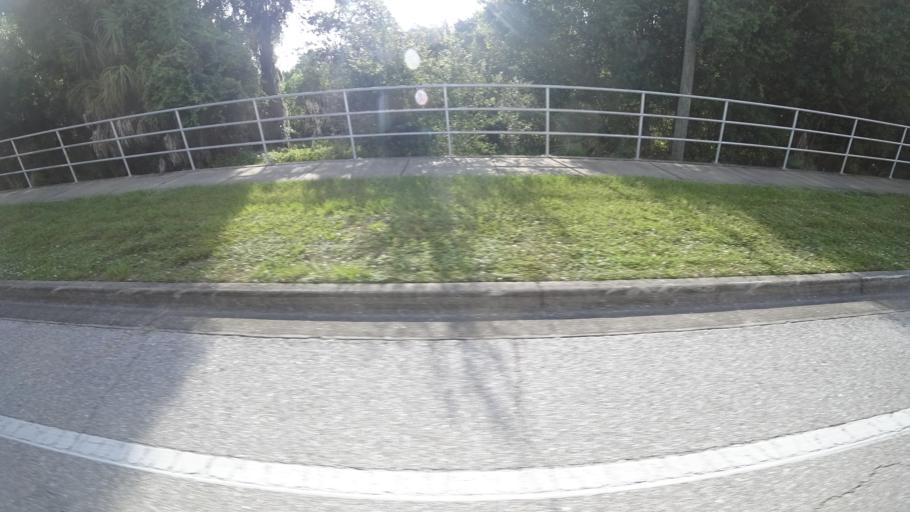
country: US
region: Florida
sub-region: Sarasota County
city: The Meadows
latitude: 27.3925
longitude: -82.4630
